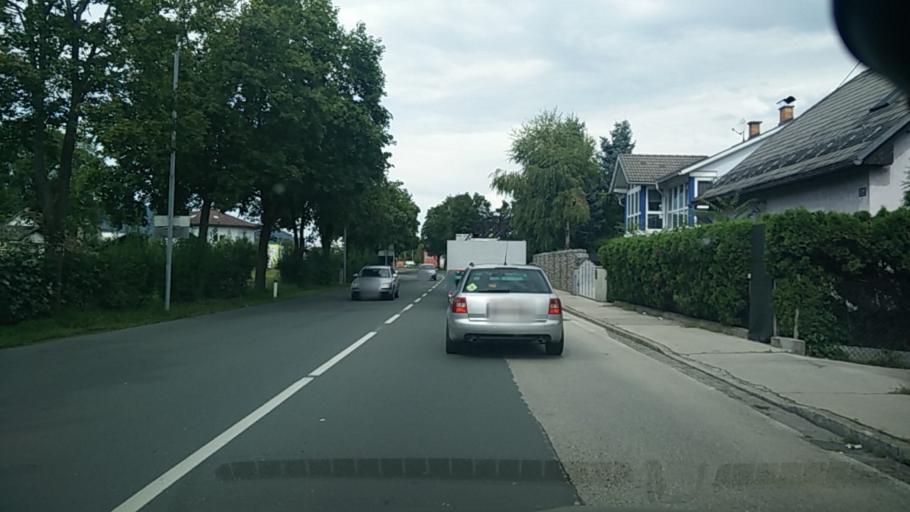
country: AT
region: Carinthia
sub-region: Klagenfurt am Woerthersee
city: Klagenfurt am Woerthersee
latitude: 46.6075
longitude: 14.2979
